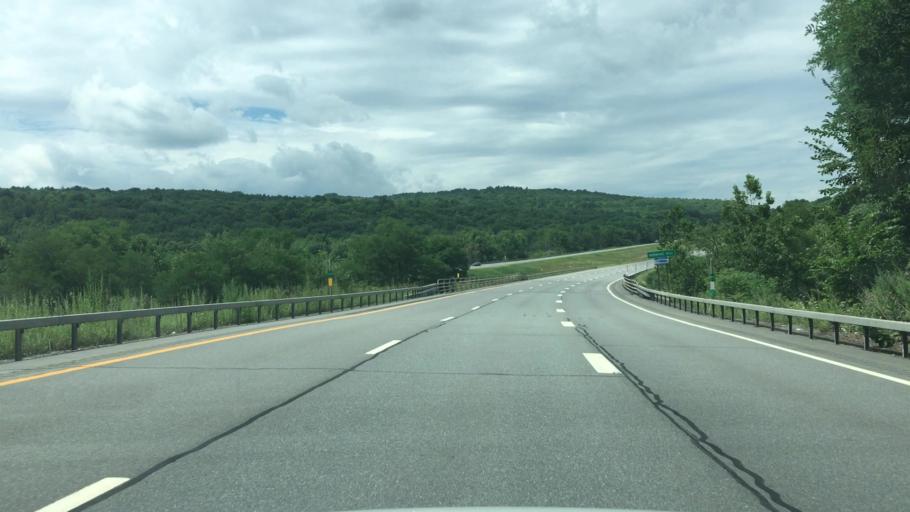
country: US
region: New York
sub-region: Albany County
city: Altamont
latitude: 42.7751
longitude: -74.0517
